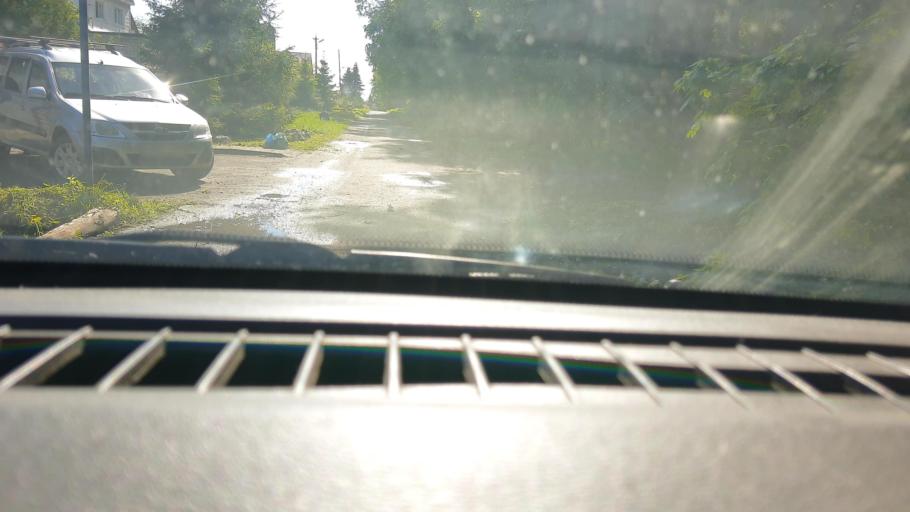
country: RU
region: Nizjnij Novgorod
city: Afonino
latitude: 56.1996
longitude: 44.0290
